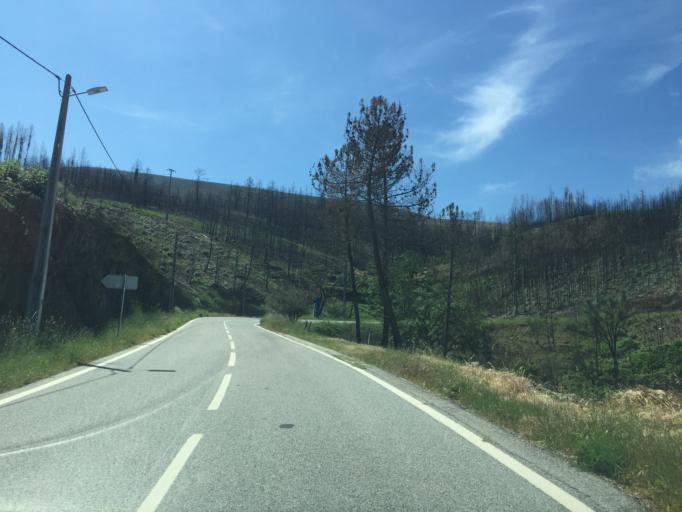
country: PT
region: Coimbra
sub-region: Pampilhosa da Serra
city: Pampilhosa da Serra
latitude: 40.0418
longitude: -7.9548
